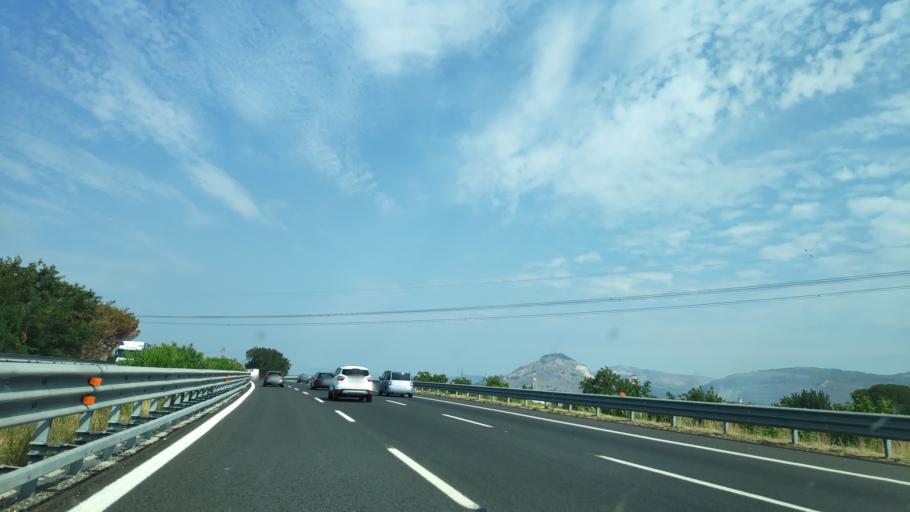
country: IT
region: Campania
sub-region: Provincia di Caserta
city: Montedecoro
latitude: 41.0055
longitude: 14.4036
